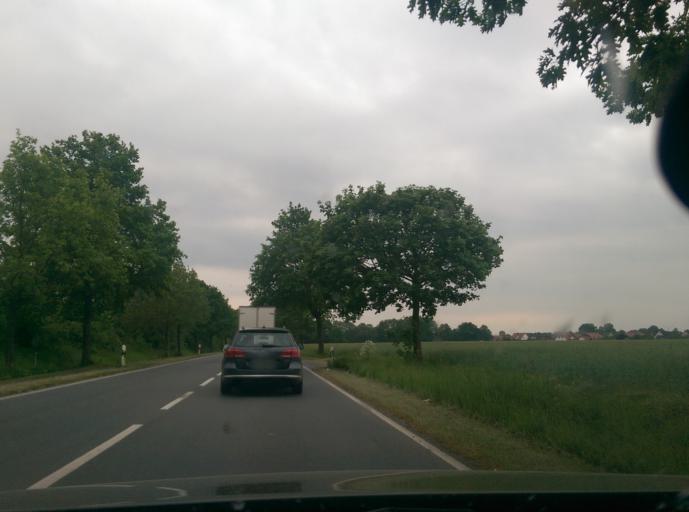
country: DE
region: Lower Saxony
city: Garbsen-Mitte
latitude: 52.4457
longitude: 9.5930
